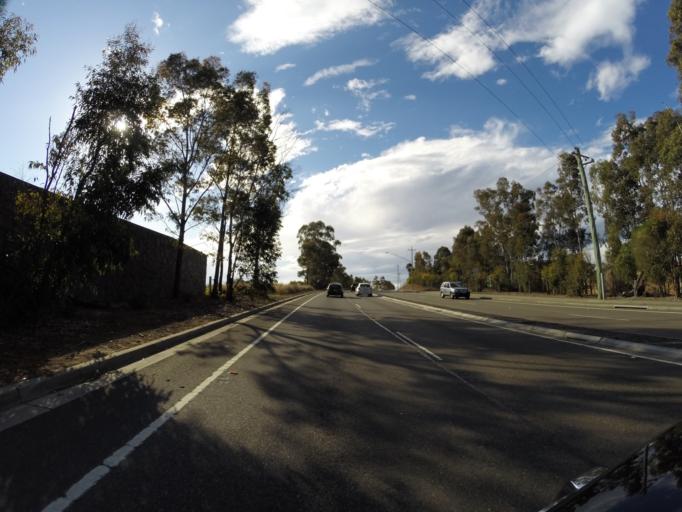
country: AU
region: New South Wales
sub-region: Fairfield
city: Cecil Park
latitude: -33.8655
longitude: 150.8704
